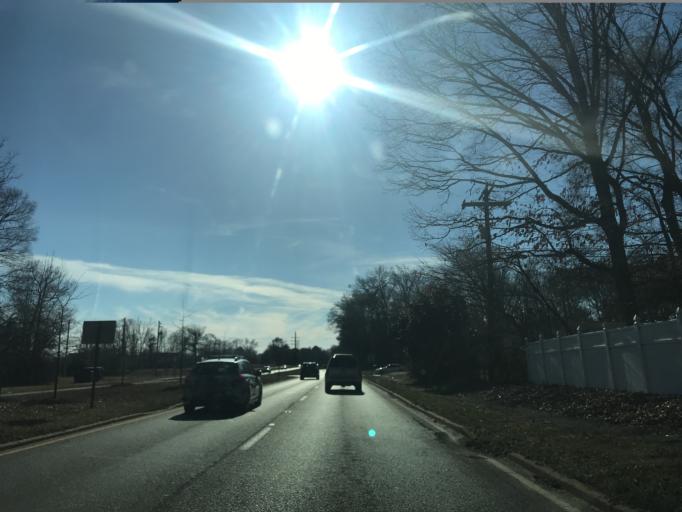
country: US
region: Maryland
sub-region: Charles County
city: Saint Charles
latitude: 38.5980
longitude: -76.9106
